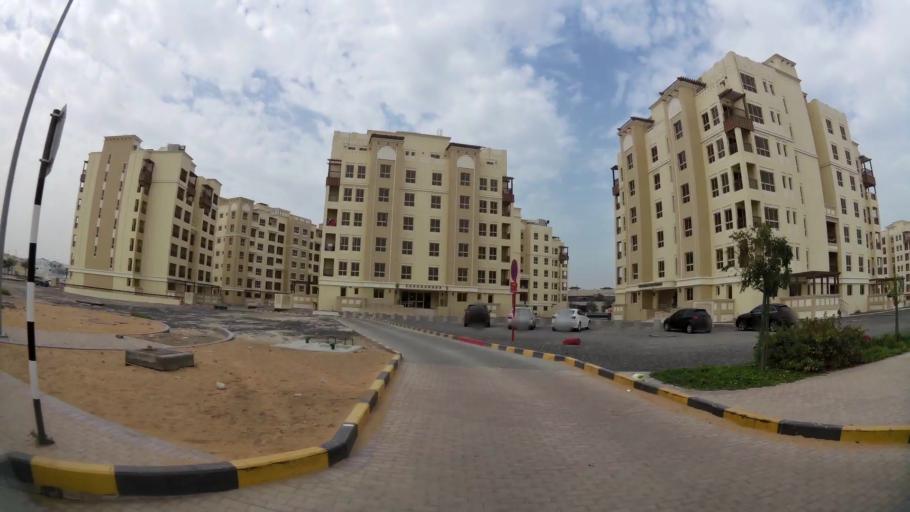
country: AE
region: Abu Dhabi
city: Abu Dhabi
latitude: 24.3111
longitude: 54.6241
